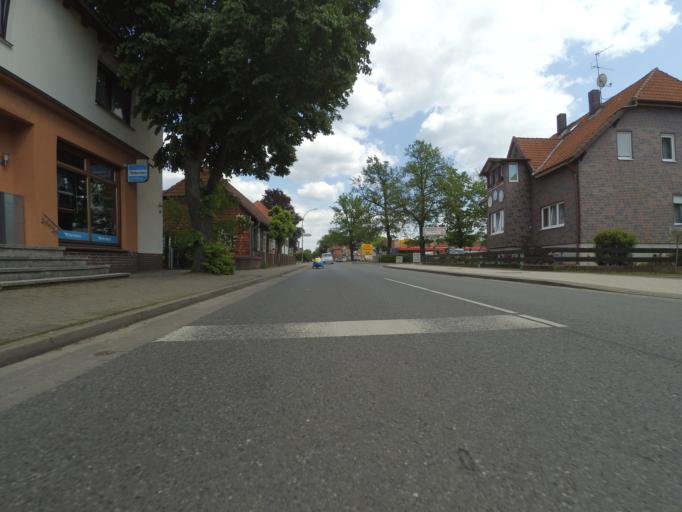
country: DE
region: Lower Saxony
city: Meinersen
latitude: 52.4743
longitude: 10.3535
